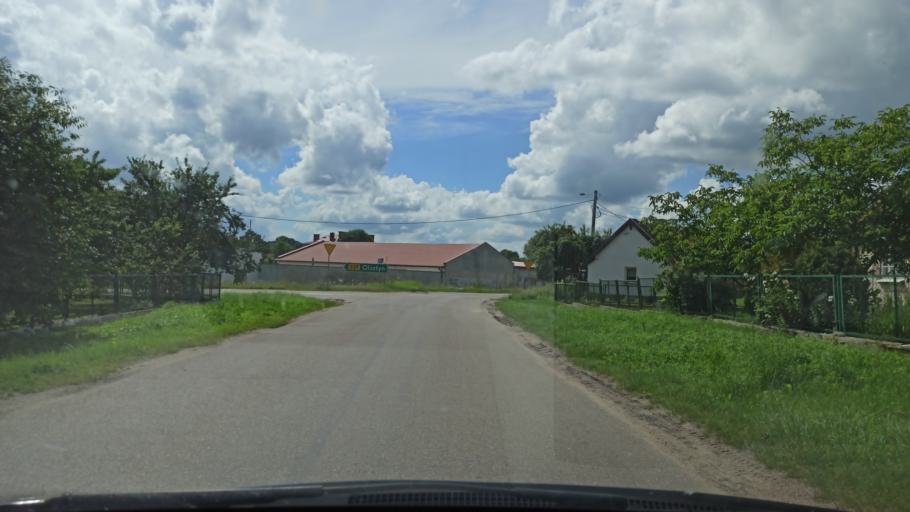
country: PL
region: Warmian-Masurian Voivodeship
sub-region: Powiat ostrodzki
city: Morag
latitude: 53.8564
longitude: 19.9835
